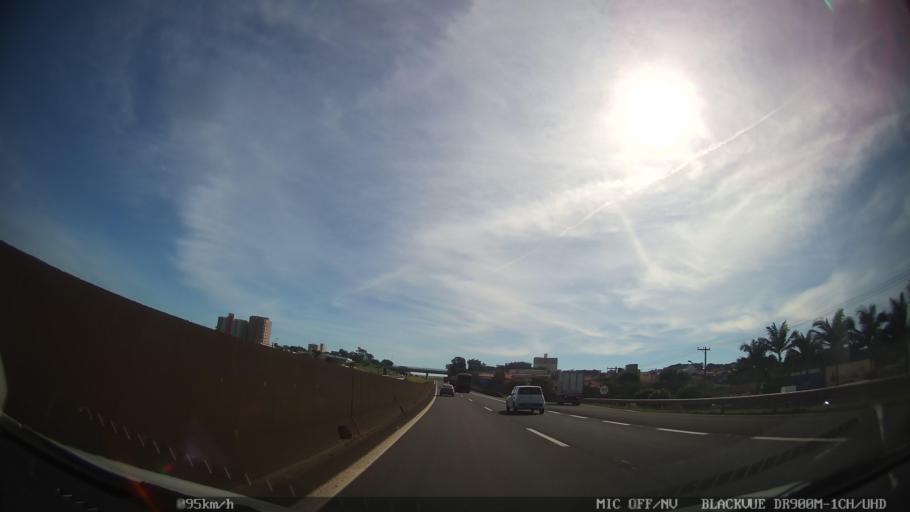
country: BR
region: Sao Paulo
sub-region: Araras
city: Araras
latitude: -22.3610
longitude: -47.3946
